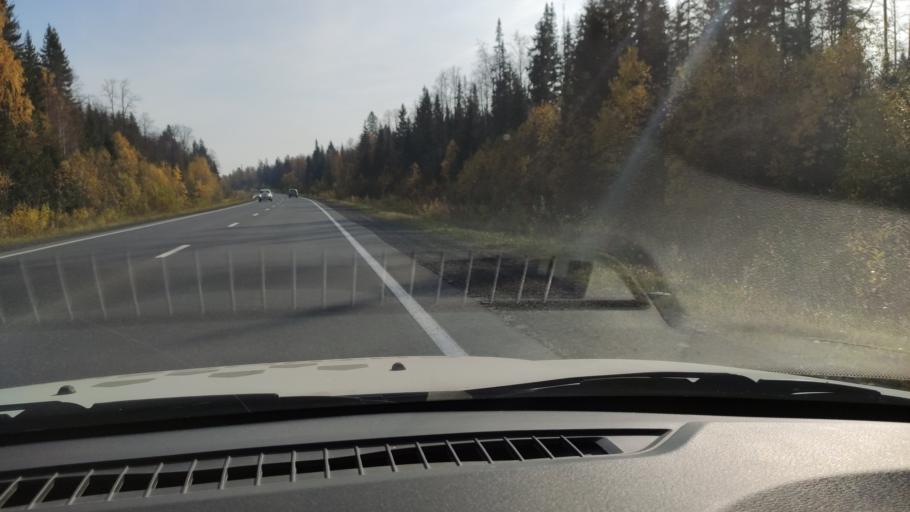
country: RU
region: Perm
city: Novyye Lyady
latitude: 58.0313
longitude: 56.4846
